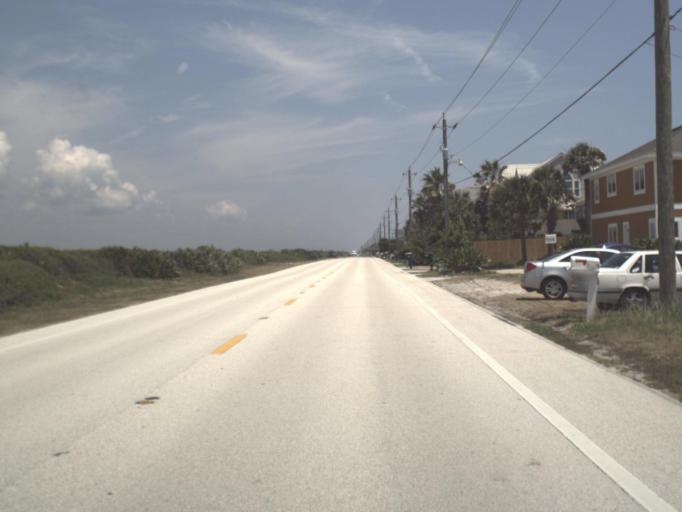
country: US
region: Florida
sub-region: Saint Johns County
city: Villano Beach
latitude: 30.0097
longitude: -81.3200
